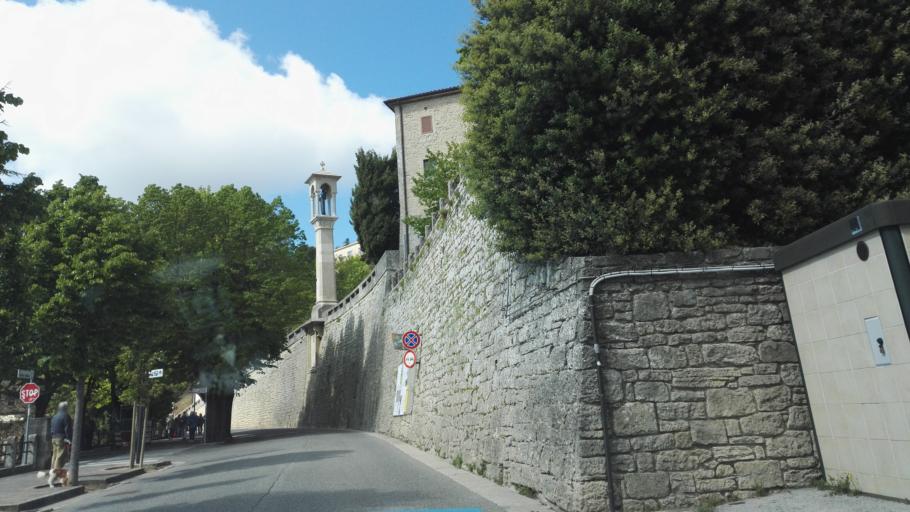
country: SM
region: San Marino
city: San Marino
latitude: 43.9330
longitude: 12.4484
